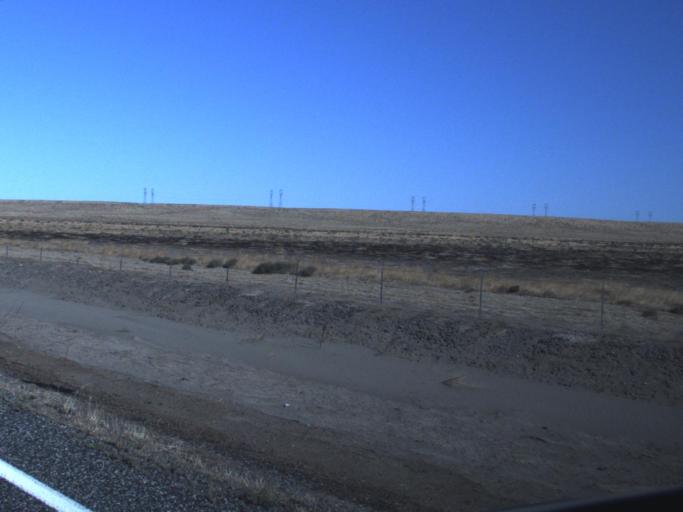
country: US
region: Washington
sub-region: Grant County
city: Desert Aire
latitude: 46.5474
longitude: -119.6914
